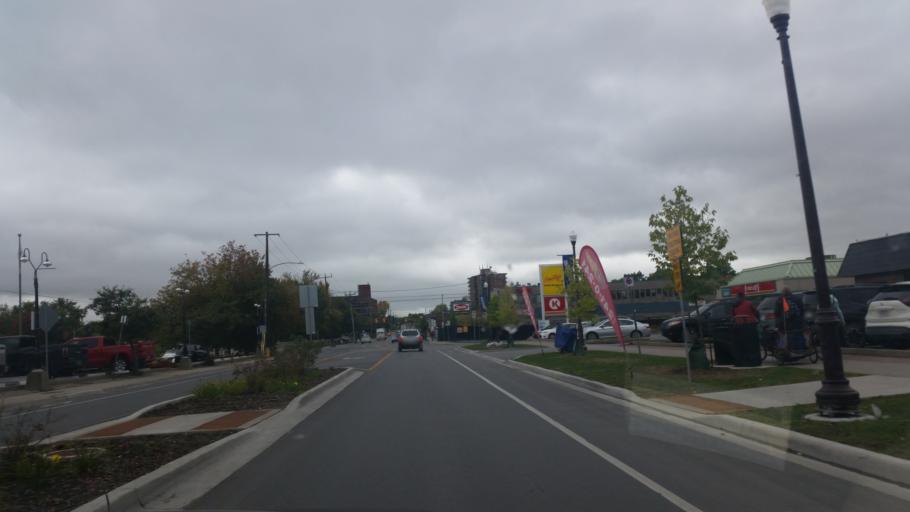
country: CA
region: Ontario
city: Peterborough
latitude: 44.2978
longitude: -78.3196
